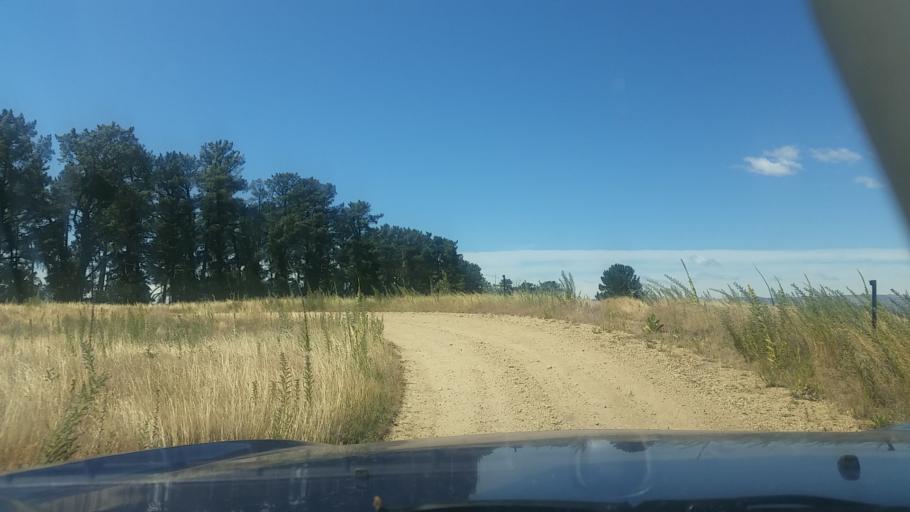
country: NZ
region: Otago
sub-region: Queenstown-Lakes District
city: Wanaka
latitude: -45.1504
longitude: 169.3994
